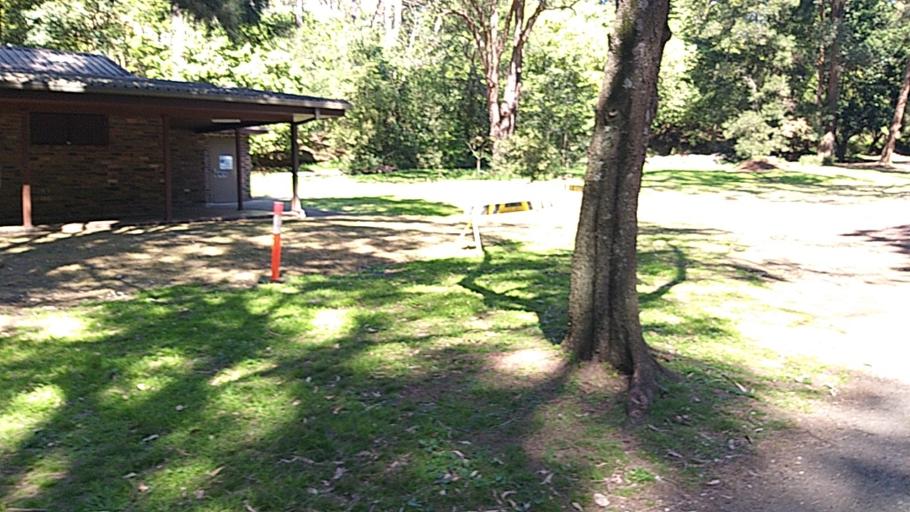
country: AU
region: New South Wales
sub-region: Ryde
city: East Ryde
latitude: -33.8158
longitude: 151.1337
